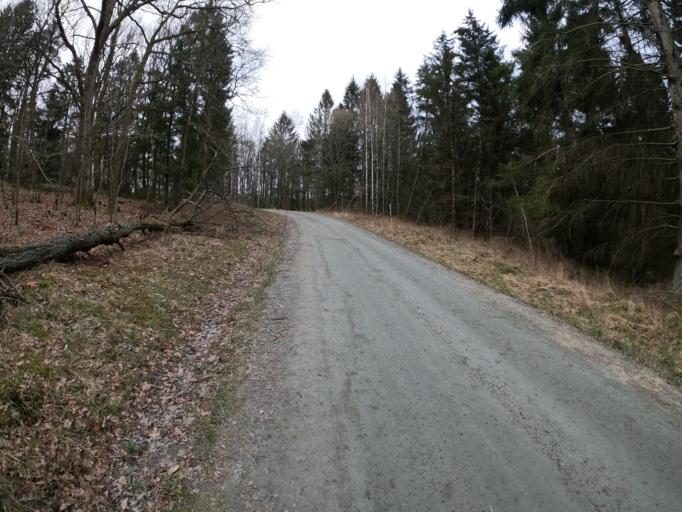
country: SE
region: Vaestra Goetaland
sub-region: Harryda Kommun
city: Molnlycke
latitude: 57.6315
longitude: 12.1046
